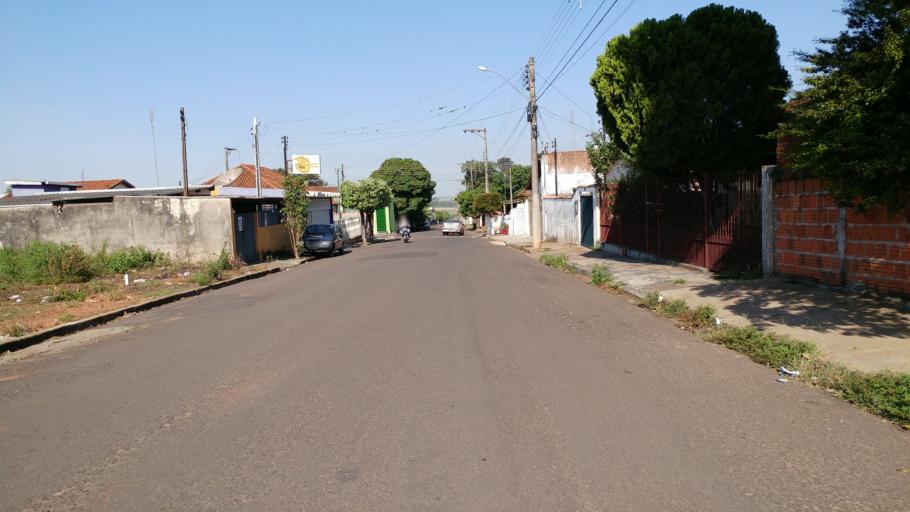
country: BR
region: Sao Paulo
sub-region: Paraguacu Paulista
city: Paraguacu Paulista
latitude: -22.4177
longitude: -50.5718
